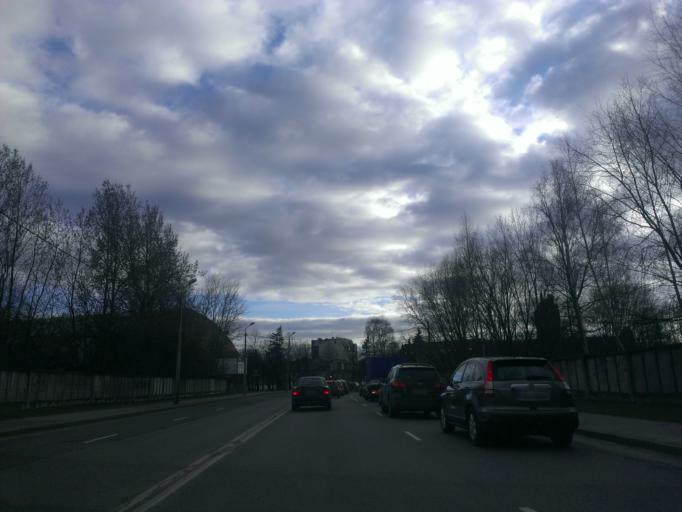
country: LV
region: Riga
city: Riga
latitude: 56.9636
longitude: 24.1142
